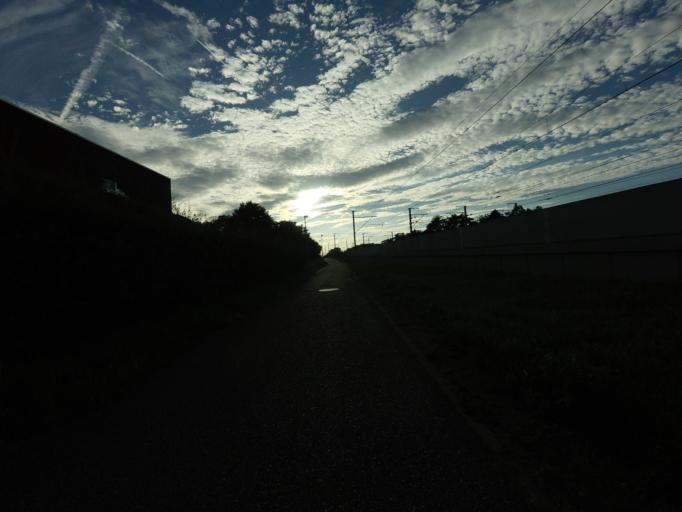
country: BE
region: Flanders
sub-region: Provincie Vlaams-Brabant
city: Herent
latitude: 50.9040
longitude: 4.6804
